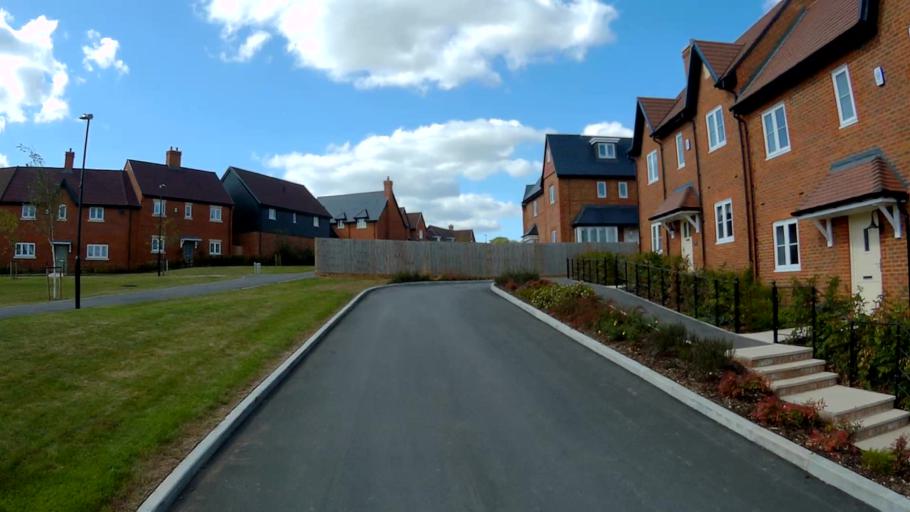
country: GB
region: England
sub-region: Bracknell Forest
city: Bracknell
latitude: 51.4296
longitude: -0.7602
